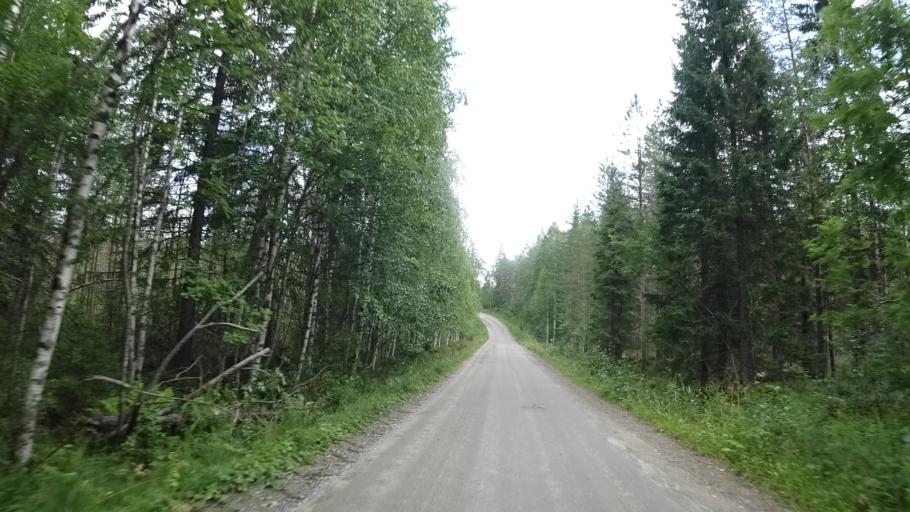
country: FI
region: North Karelia
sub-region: Joensuu
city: Ilomantsi
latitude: 62.9217
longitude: 31.3483
